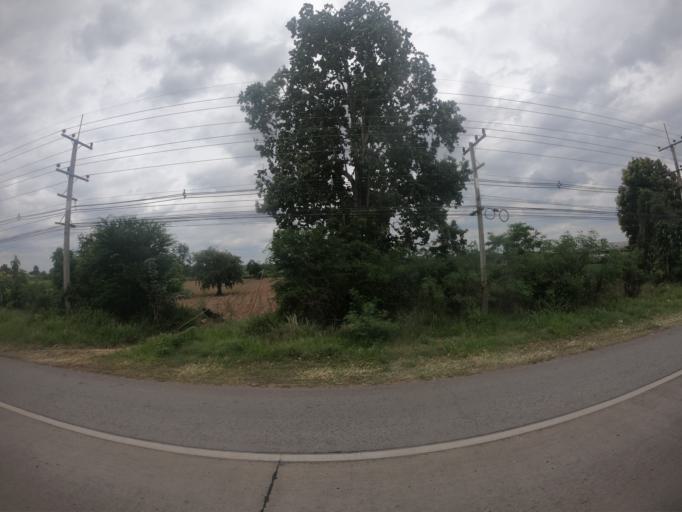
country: TH
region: Nakhon Ratchasima
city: Chok Chai
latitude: 14.7925
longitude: 102.1683
